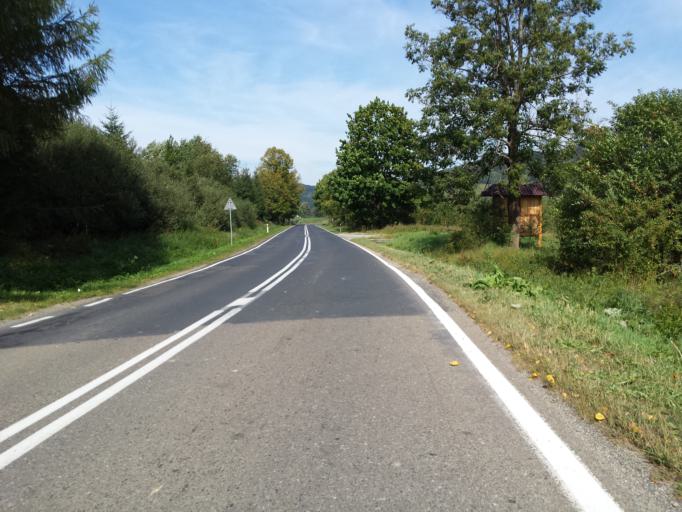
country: PL
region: Subcarpathian Voivodeship
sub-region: Powiat leski
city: Baligrod
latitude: 49.3508
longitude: 22.2889
